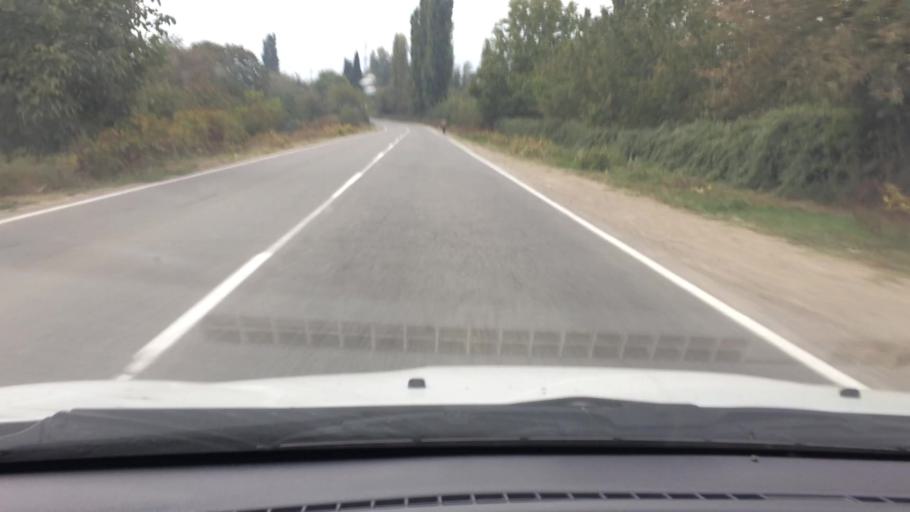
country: GE
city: Naghvarevi
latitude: 41.3001
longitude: 44.7893
